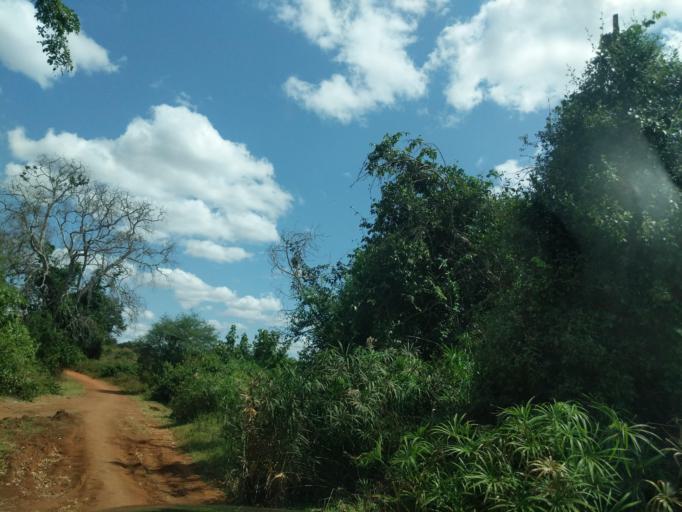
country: TZ
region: Tanga
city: Chanika
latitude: -5.5176
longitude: 38.3604
